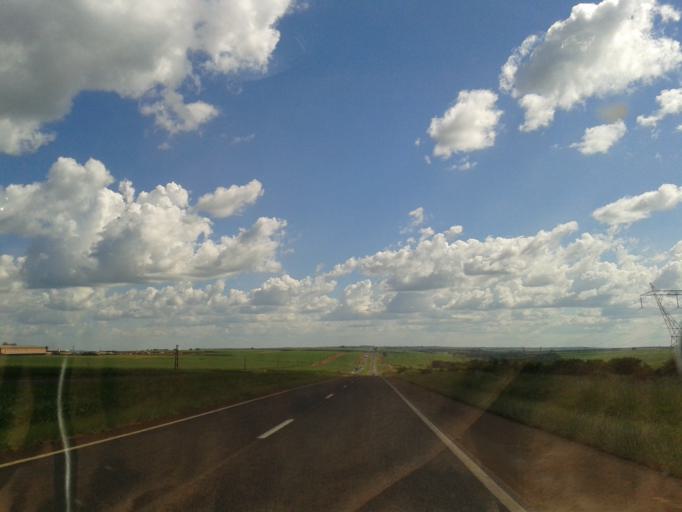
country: BR
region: Goias
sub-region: Goiatuba
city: Goiatuba
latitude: -17.9099
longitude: -49.2386
